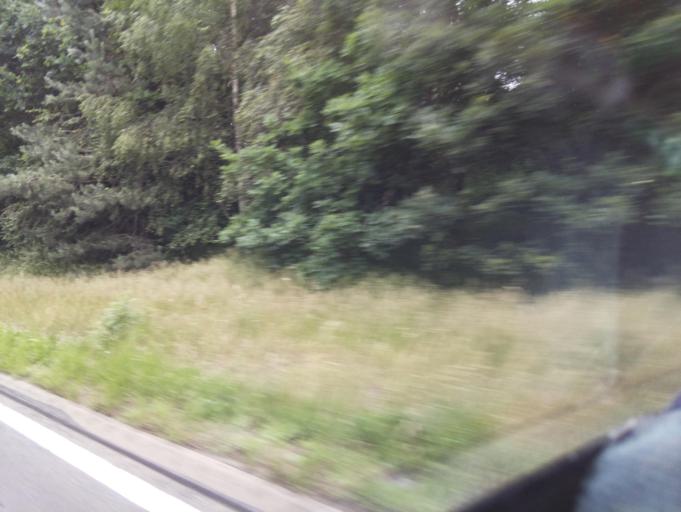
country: GB
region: England
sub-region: District of Rutland
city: Ridlington
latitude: 52.5951
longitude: -0.7688
